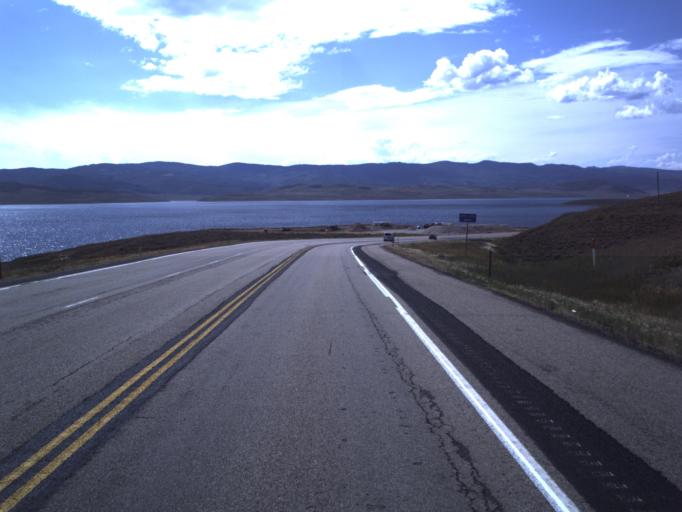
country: US
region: Utah
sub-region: Wasatch County
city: Heber
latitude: 40.1968
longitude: -111.0988
